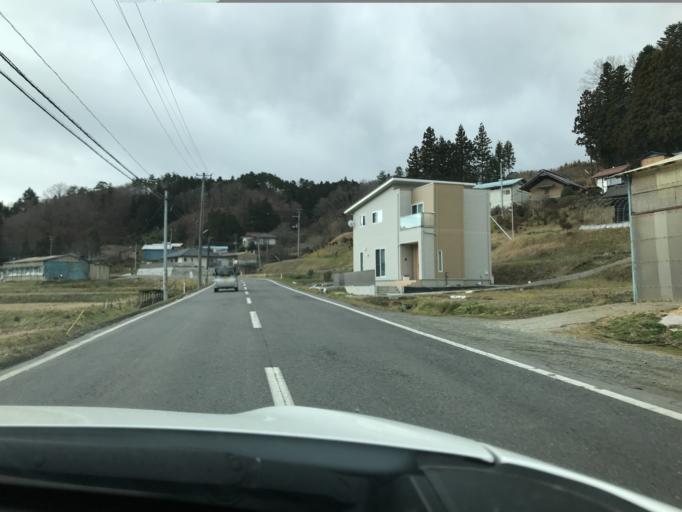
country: JP
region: Fukushima
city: Funehikimachi-funehiki
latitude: 37.4211
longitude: 140.5839
